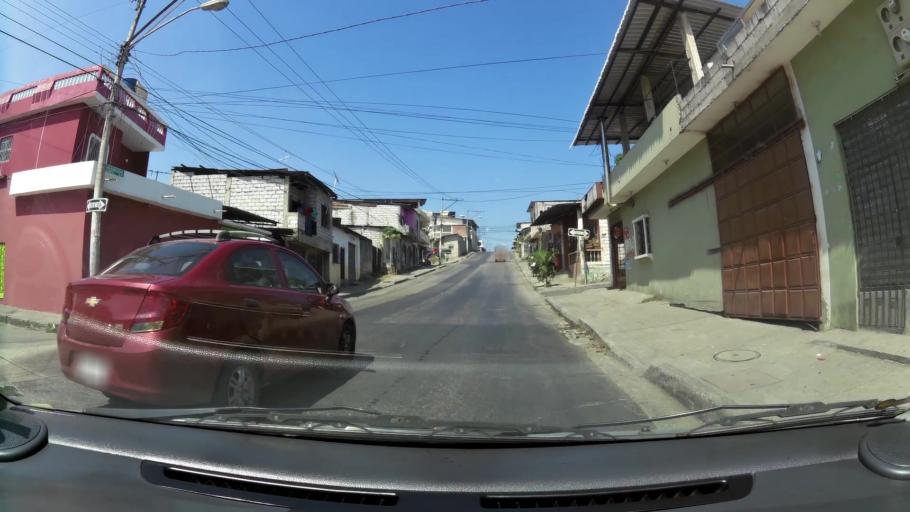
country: EC
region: Guayas
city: Guayaquil
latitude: -2.1280
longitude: -79.9189
